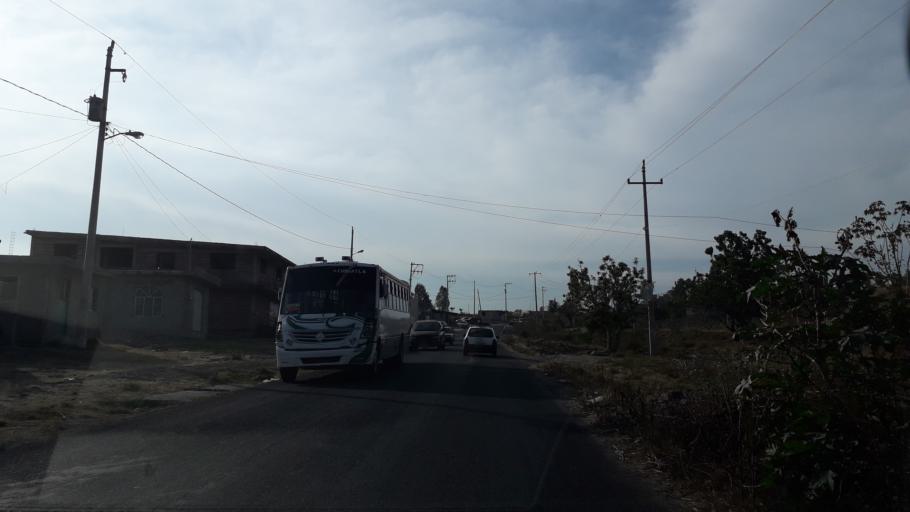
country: MX
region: Puebla
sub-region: Puebla
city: San Andres Azumiatla
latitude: 18.9138
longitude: -98.2435
